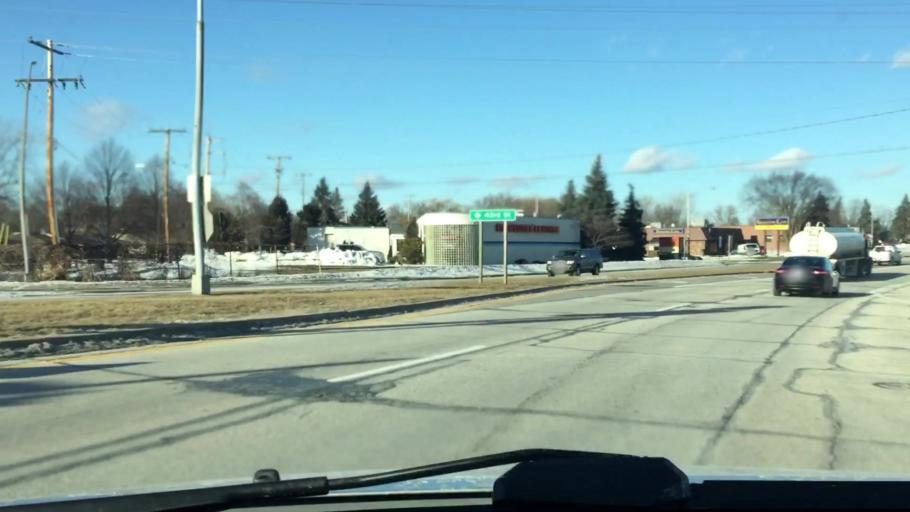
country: US
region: Wisconsin
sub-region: Milwaukee County
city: Greendale
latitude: 42.9626
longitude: -87.9683
